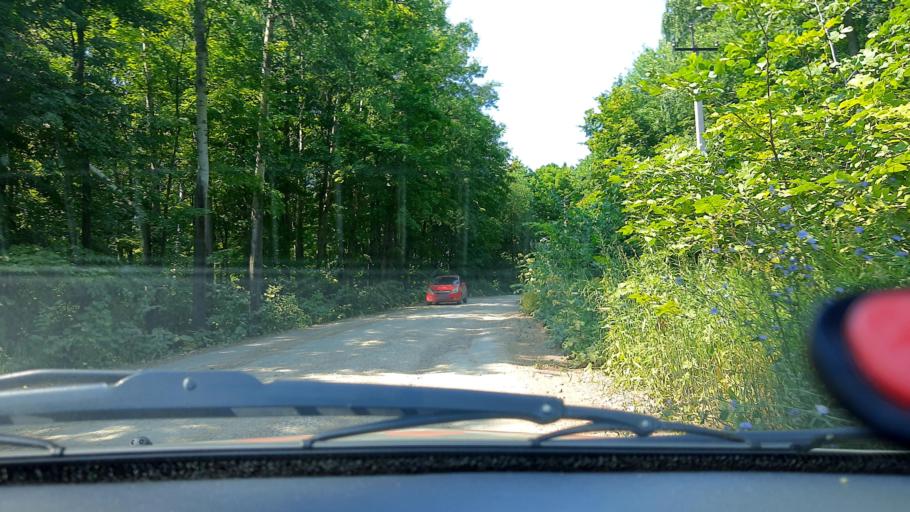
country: RU
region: Bashkortostan
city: Karmaskaly
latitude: 54.3868
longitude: 55.9033
